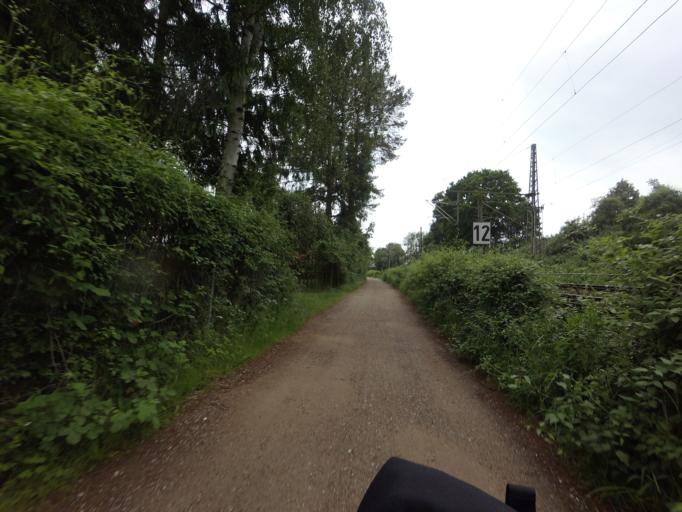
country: DE
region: Schleswig-Holstein
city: Bad Schwartau
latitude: 53.9064
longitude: 10.6926
